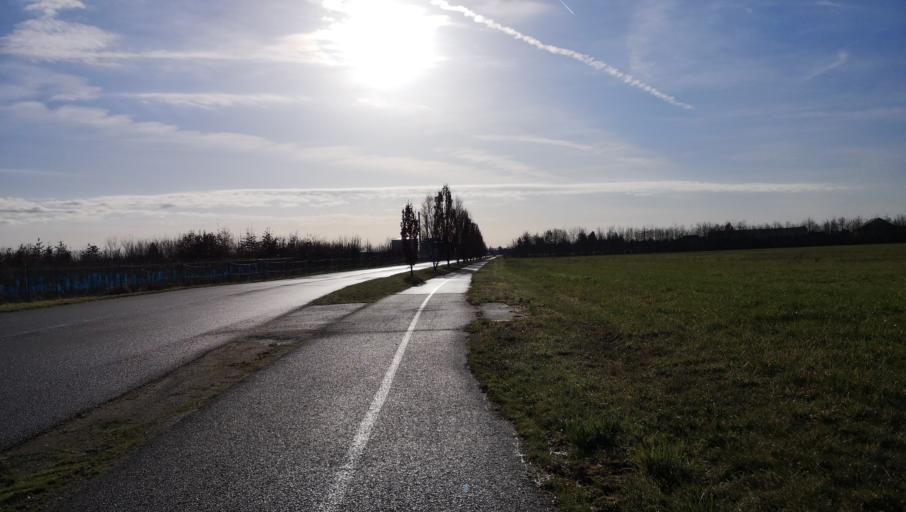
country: FR
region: Centre
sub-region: Departement du Loiret
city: Saint-Denis-en-Val
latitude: 47.8776
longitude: 1.9790
